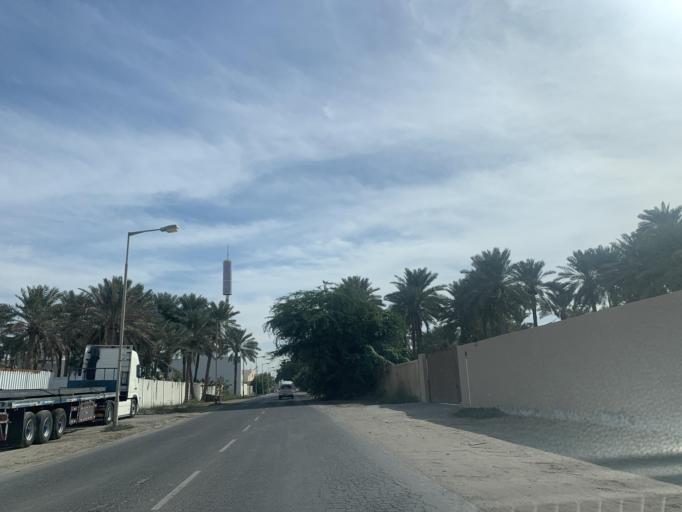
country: BH
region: Central Governorate
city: Madinat Hamad
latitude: 26.1243
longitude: 50.4720
